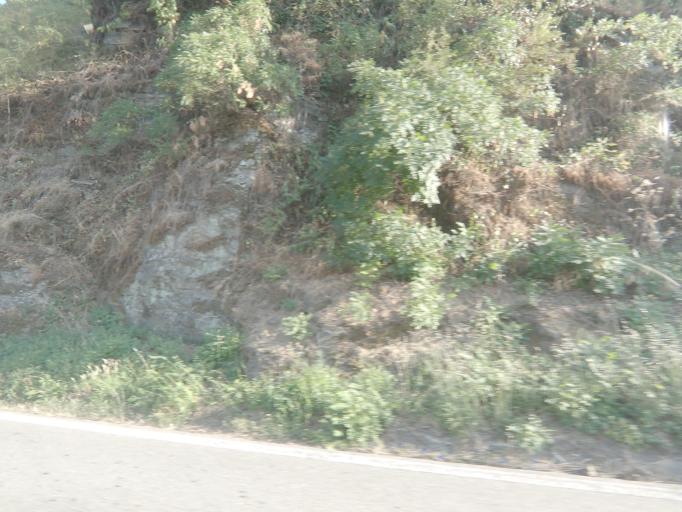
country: PT
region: Vila Real
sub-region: Peso da Regua
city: Peso da Regua
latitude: 41.1507
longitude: -7.7601
